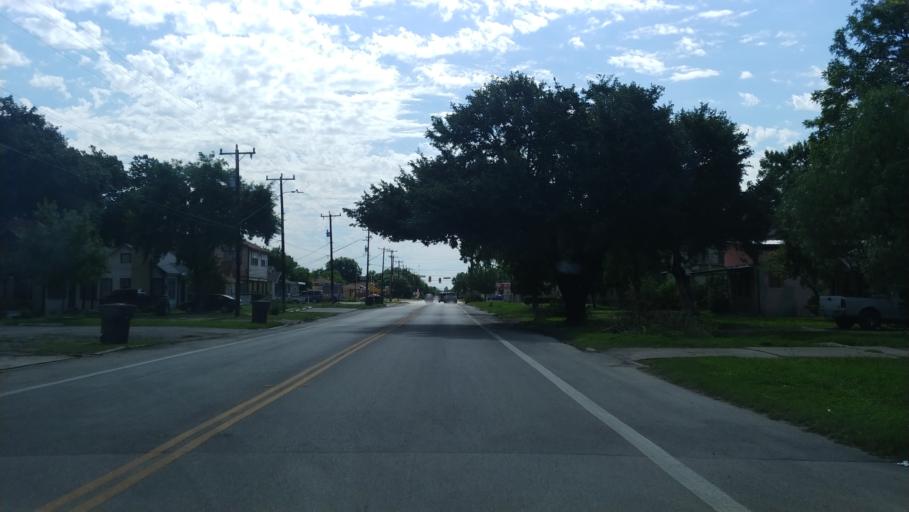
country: US
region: Texas
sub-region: Bexar County
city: San Antonio
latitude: 29.4497
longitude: -98.5263
